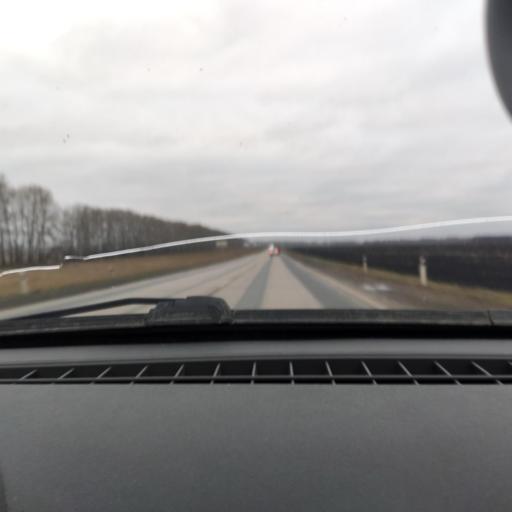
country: RU
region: Bashkortostan
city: Karmaskaly
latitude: 54.3852
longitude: 56.1701
